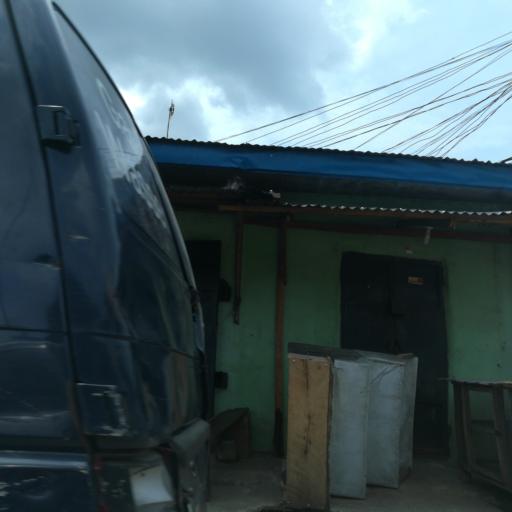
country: NG
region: Rivers
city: Port Harcourt
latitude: 4.7759
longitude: 7.0420
